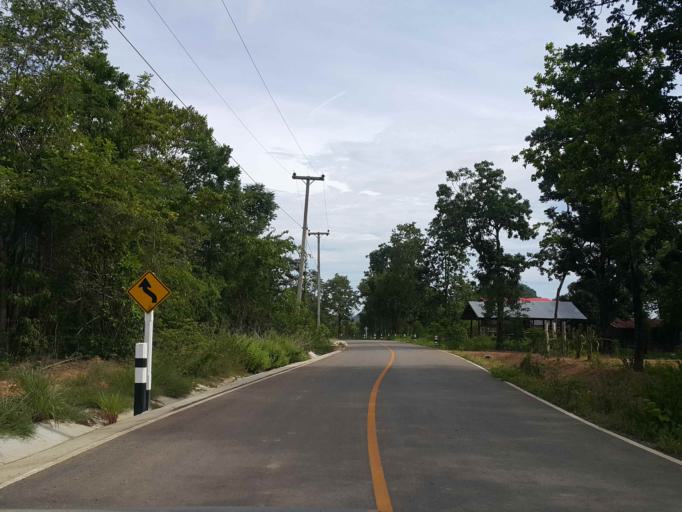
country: TH
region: Sukhothai
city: Thung Saliam
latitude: 17.2312
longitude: 99.5095
